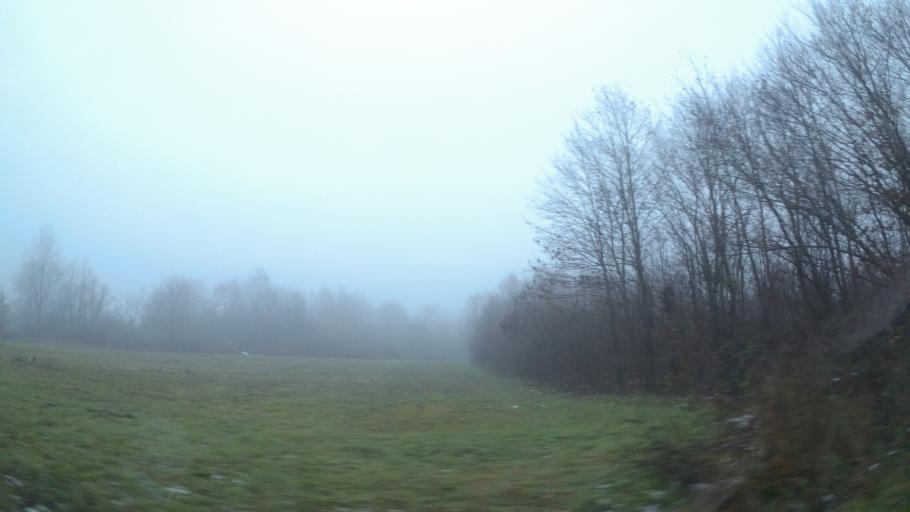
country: HR
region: Sisacko-Moslavacka
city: Glina
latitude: 45.3295
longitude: 16.0399
